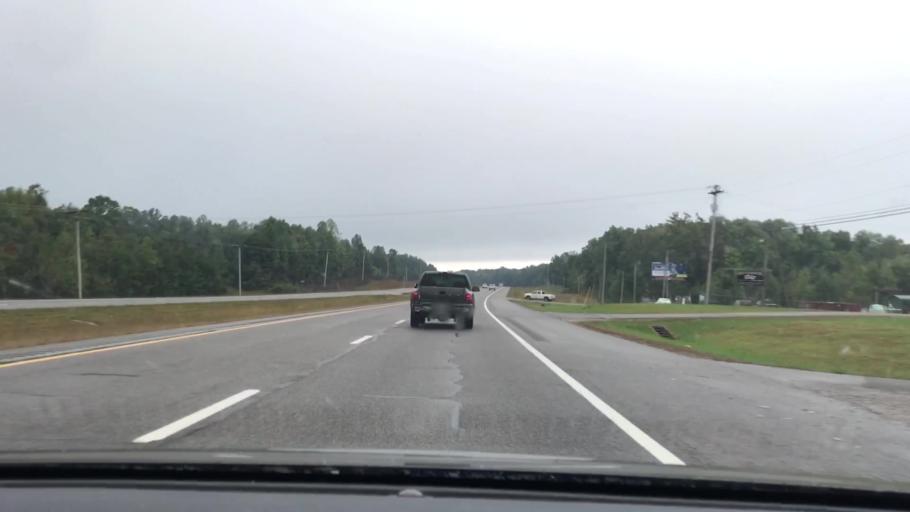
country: US
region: Tennessee
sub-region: Fentress County
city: Jamestown
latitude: 36.3618
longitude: -84.9472
